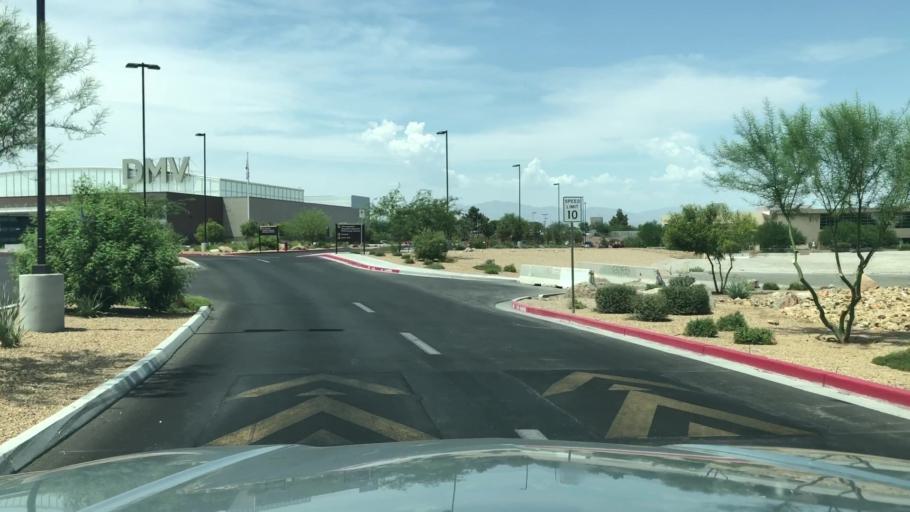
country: US
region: Nevada
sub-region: Clark County
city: Winchester
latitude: 36.1451
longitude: -115.1120
